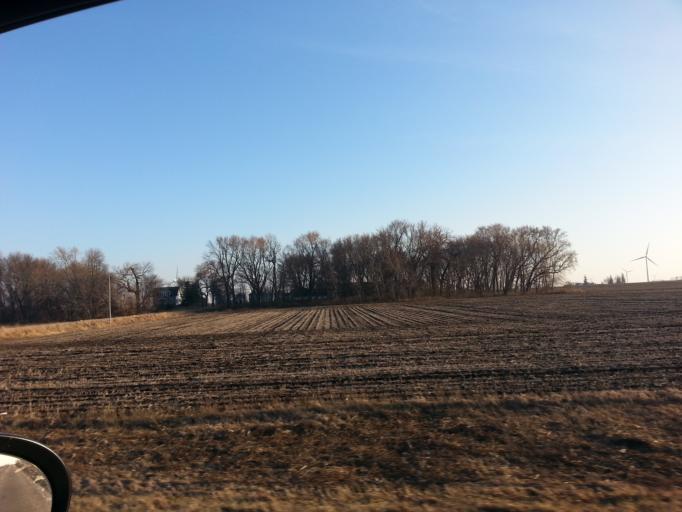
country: US
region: Iowa
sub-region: Worth County
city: Northwood
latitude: 43.4369
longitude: -93.0977
